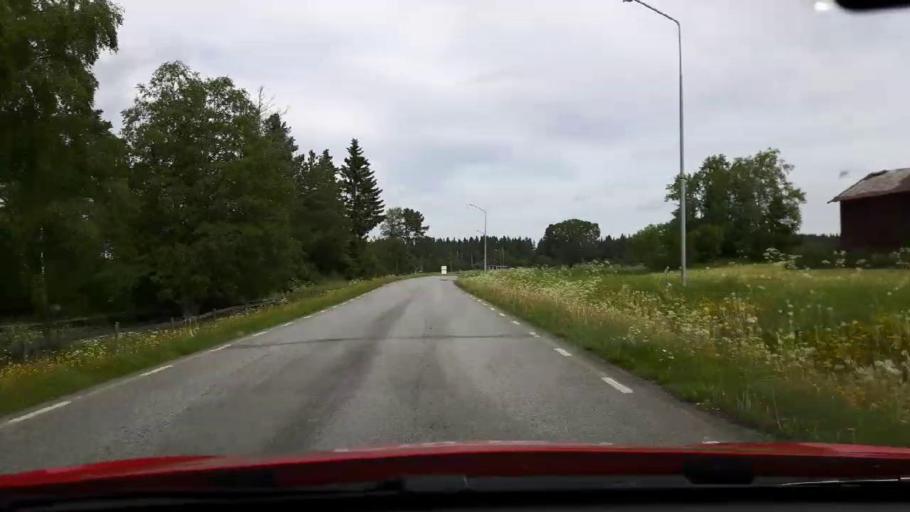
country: SE
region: Jaemtland
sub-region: OEstersunds Kommun
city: Ostersund
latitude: 63.0550
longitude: 14.4505
